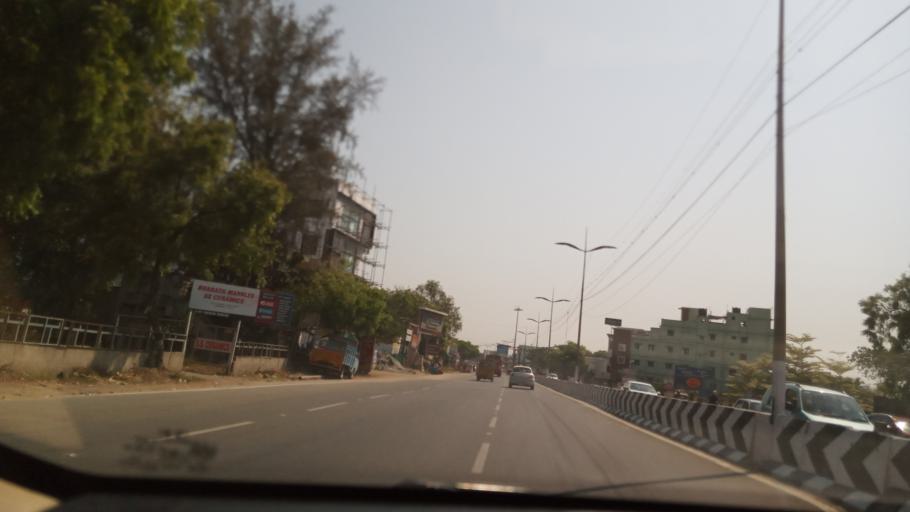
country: IN
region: Tamil Nadu
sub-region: Coimbatore
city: Irugur
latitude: 11.0458
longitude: 77.0505
